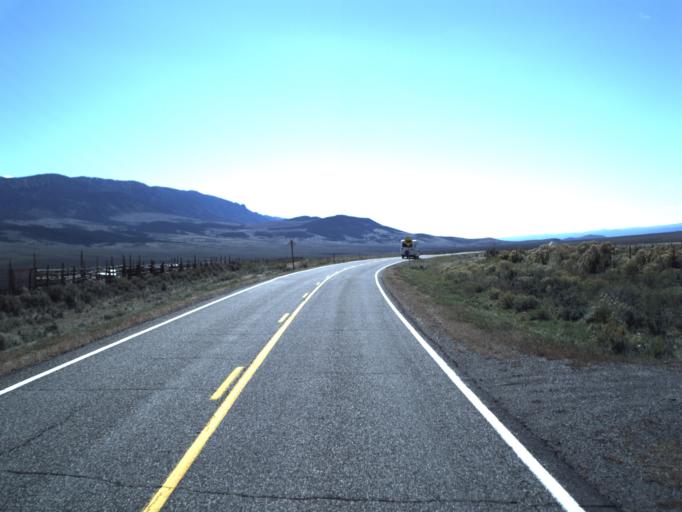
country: US
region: Utah
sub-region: Wayne County
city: Loa
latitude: 38.4237
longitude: -111.9226
